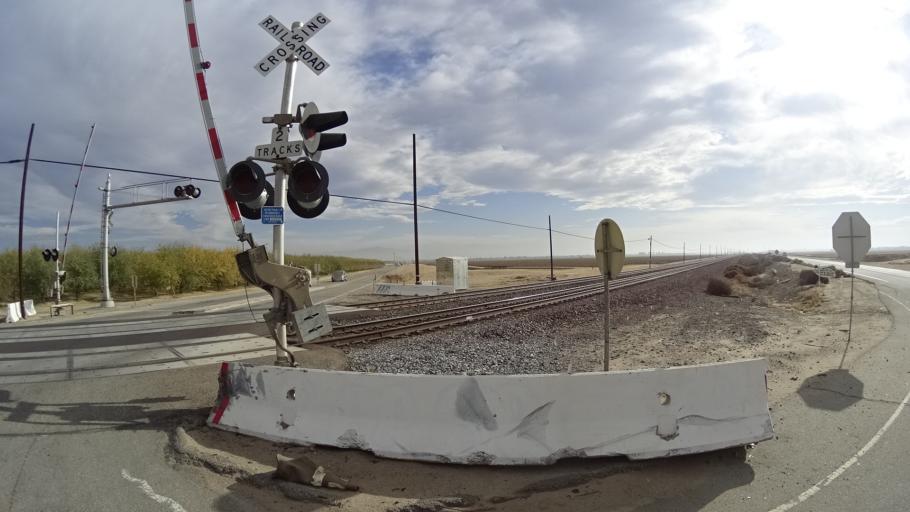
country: US
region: California
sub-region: Kern County
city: Rosedale
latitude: 35.4196
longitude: -119.1722
